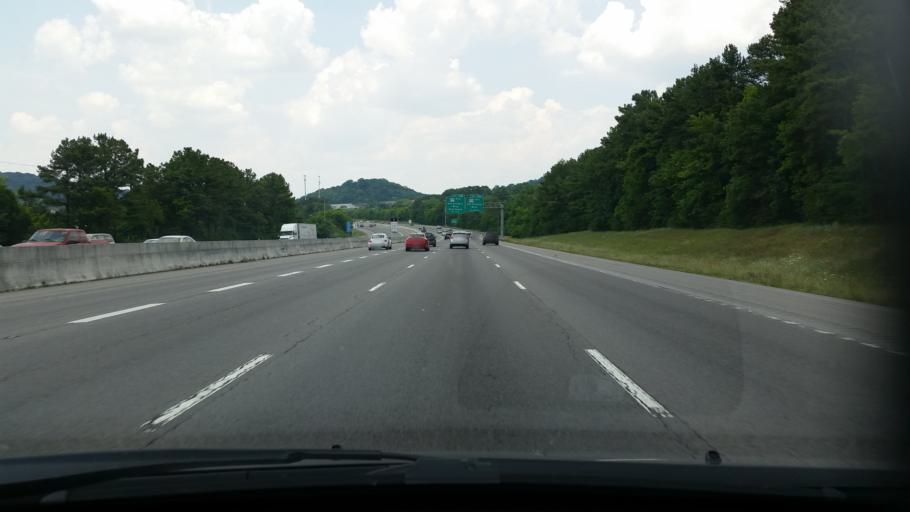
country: US
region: Tennessee
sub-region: Williamson County
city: Brentwood Estates
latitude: 36.0244
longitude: -86.7857
